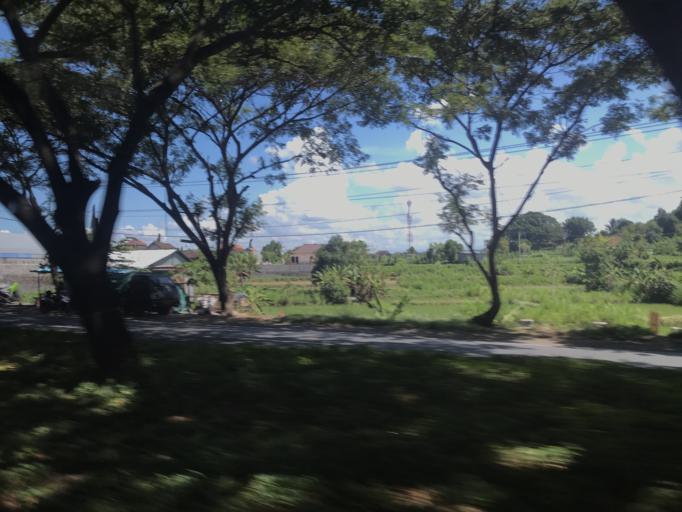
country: ID
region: Bali
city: Dawan
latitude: -8.5537
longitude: 115.4343
